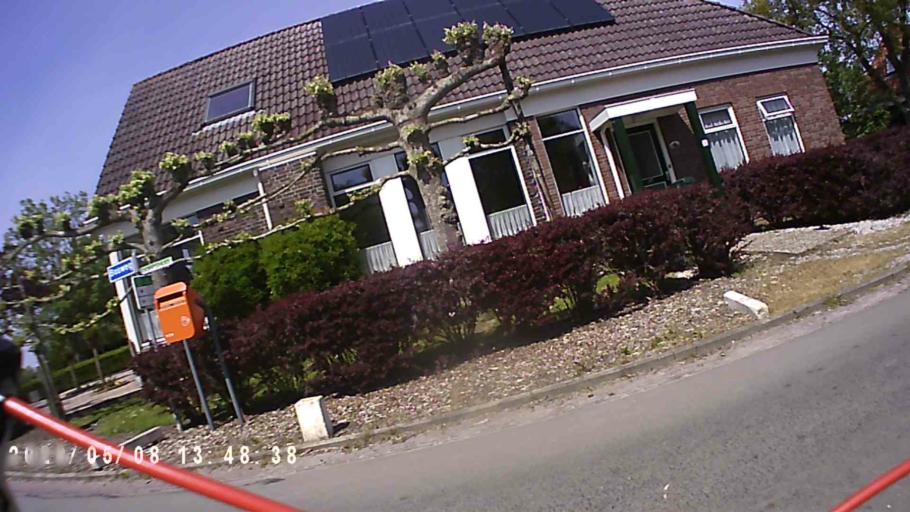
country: NL
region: Groningen
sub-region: Gemeente Appingedam
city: Appingedam
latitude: 53.3379
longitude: 6.7810
